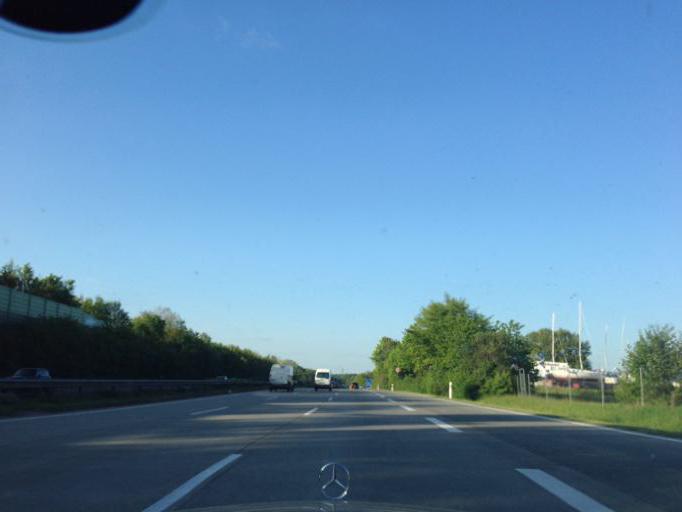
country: DE
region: Schleswig-Holstein
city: Siek
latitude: 53.6451
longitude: 10.2828
